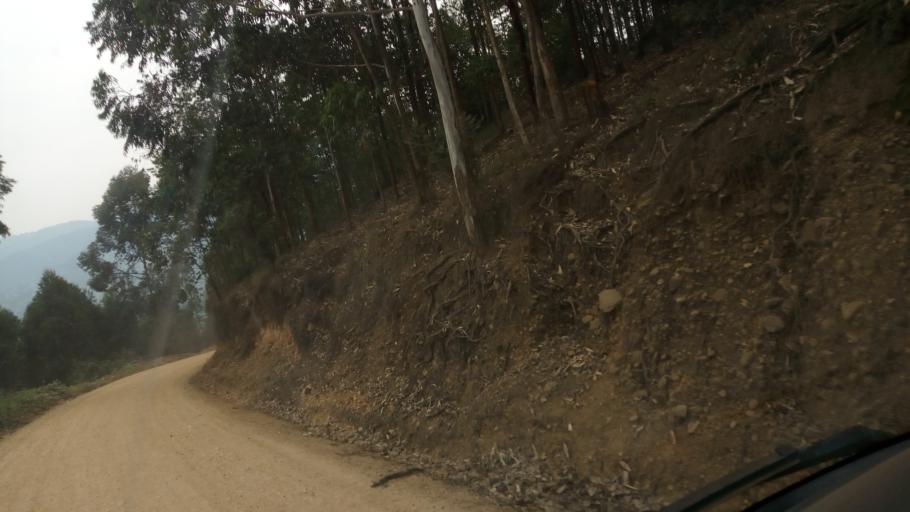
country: UG
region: Western Region
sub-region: Kanungu District
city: Kanungu
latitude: -1.1027
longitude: 29.8558
